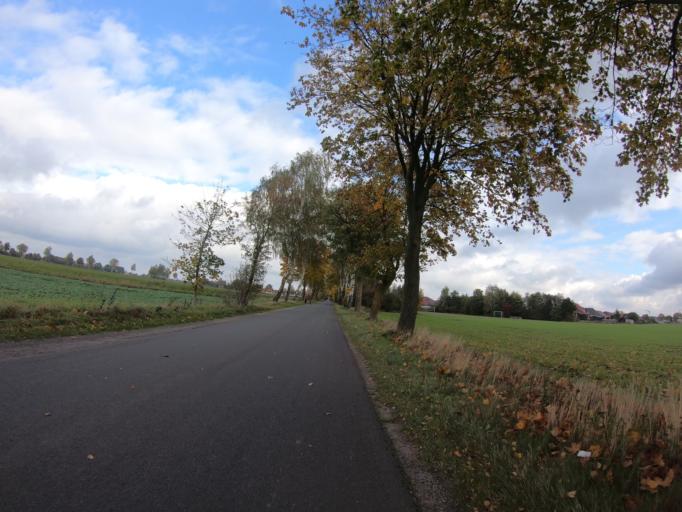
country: DE
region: Lower Saxony
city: Wahrenholz
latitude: 52.6045
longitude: 10.5920
